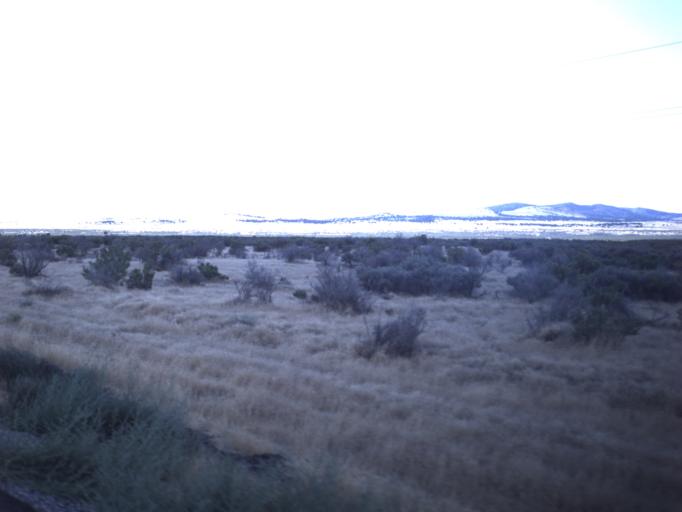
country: US
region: Utah
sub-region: Tooele County
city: Grantsville
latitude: 40.2515
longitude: -112.7022
